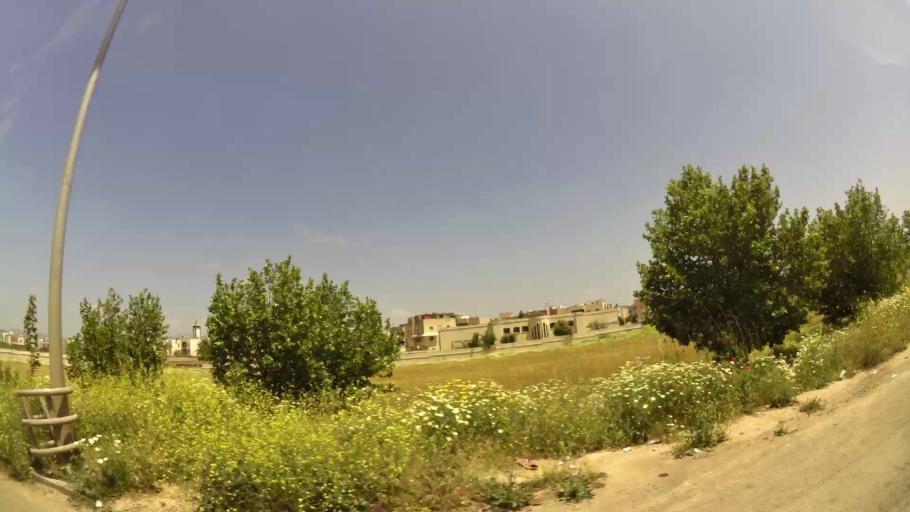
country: MA
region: Fes-Boulemane
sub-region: Fes
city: Fes
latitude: 34.0296
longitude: -5.0284
